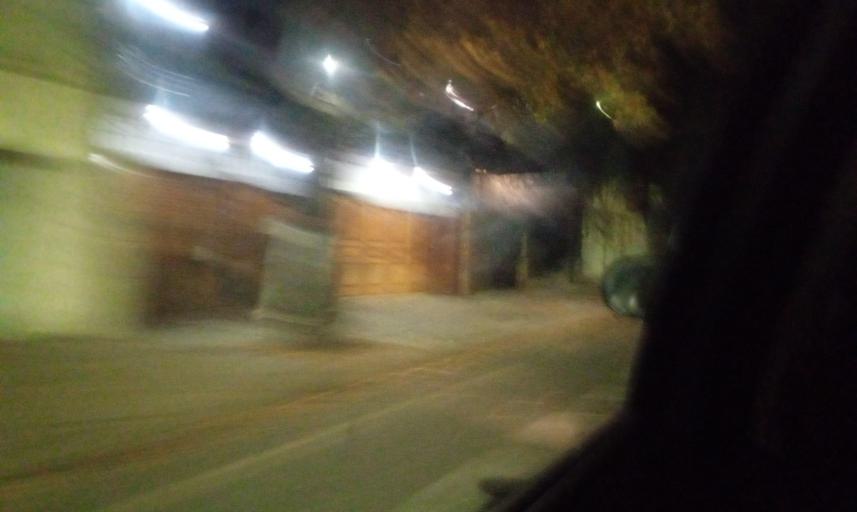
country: AR
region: Buenos Aires F.D.
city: Villa Santa Rita
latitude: -34.6176
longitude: -58.5118
